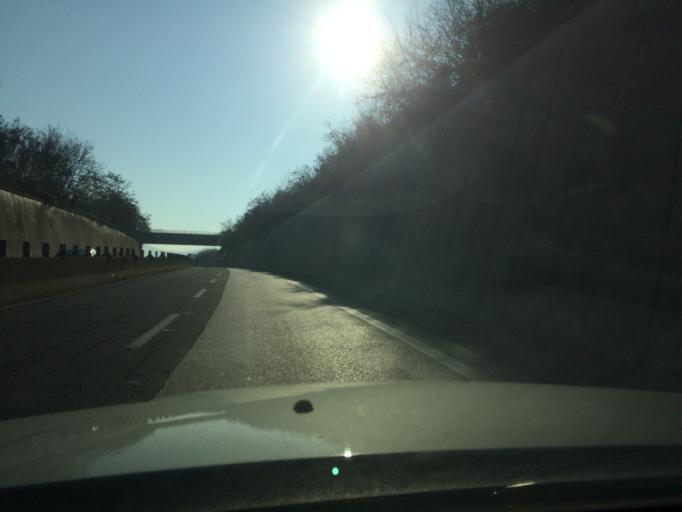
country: IT
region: Umbria
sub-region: Provincia di Perugia
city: Ponterio-Pian di Porto
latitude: 42.8271
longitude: 12.3990
